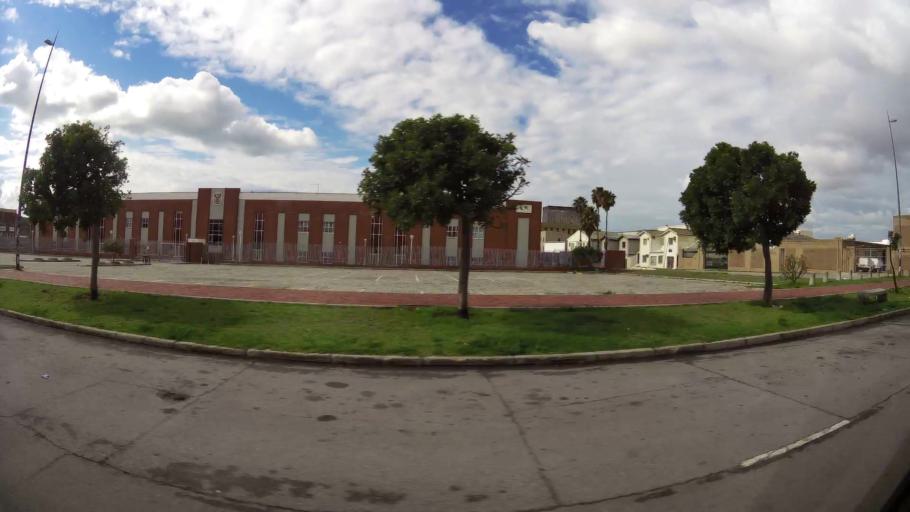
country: ZA
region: Eastern Cape
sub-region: Nelson Mandela Bay Metropolitan Municipality
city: Port Elizabeth
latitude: -33.9448
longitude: 25.6030
